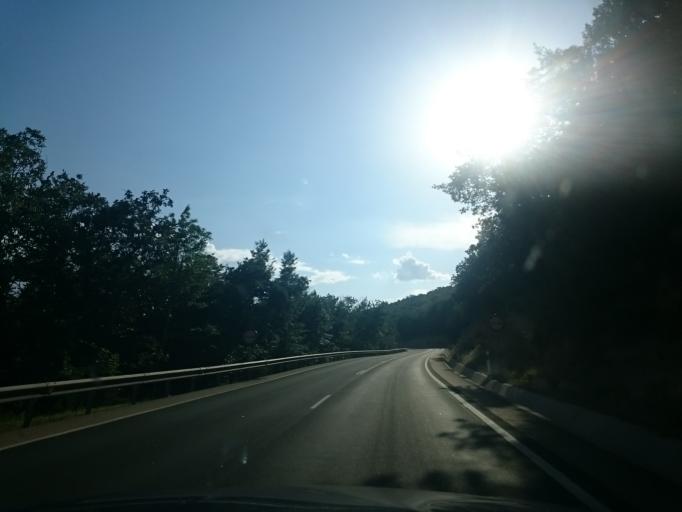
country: ES
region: Castille and Leon
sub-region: Provincia de Burgos
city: Espinosa del Camino
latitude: 42.3794
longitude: -3.3165
